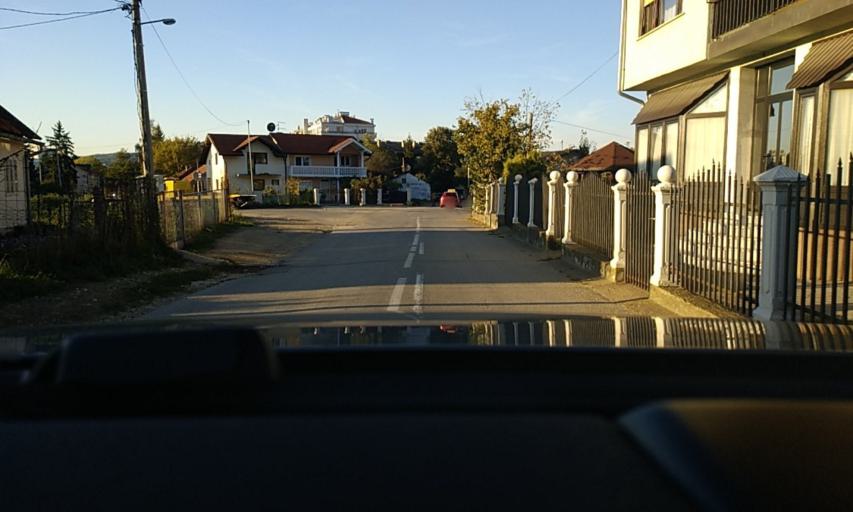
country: BA
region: Republika Srpska
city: Mejdan - Obilicevo
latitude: 44.7573
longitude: 17.1910
